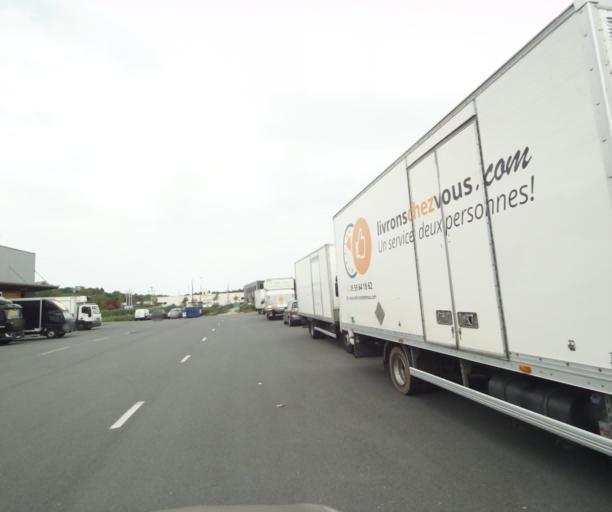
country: FR
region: Aquitaine
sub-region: Departement des Pyrenees-Atlantiques
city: Mouguerre
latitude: 43.4889
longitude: -1.4267
